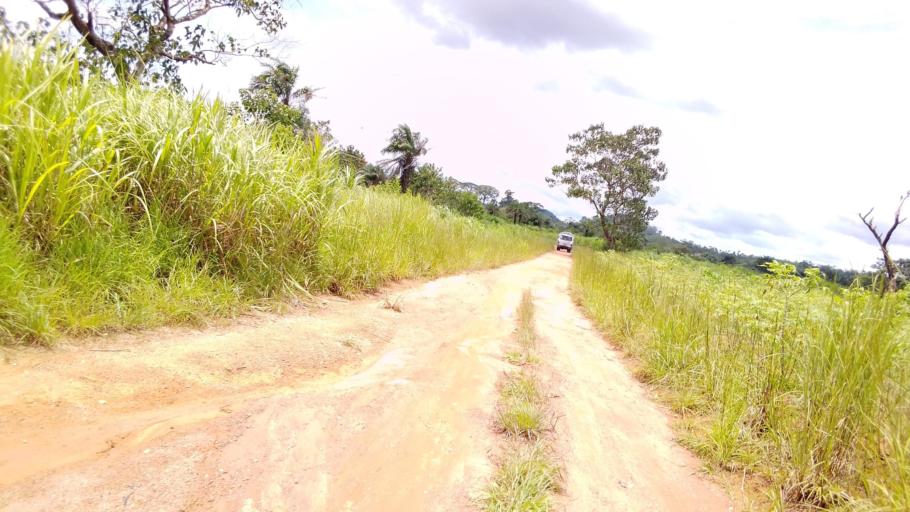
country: SL
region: Eastern Province
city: Koidu
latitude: 8.6712
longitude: -10.9540
